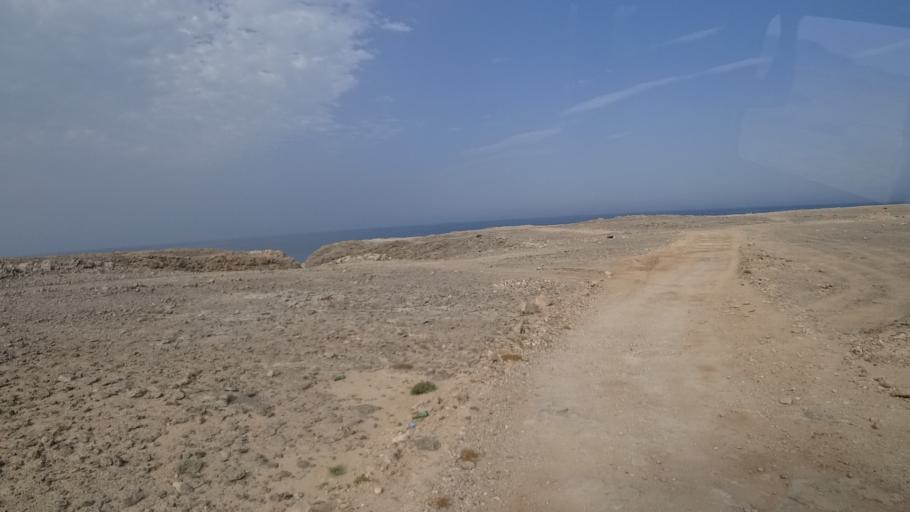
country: OM
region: Ash Sharqiyah
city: Sur
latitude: 22.4517
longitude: 59.8264
